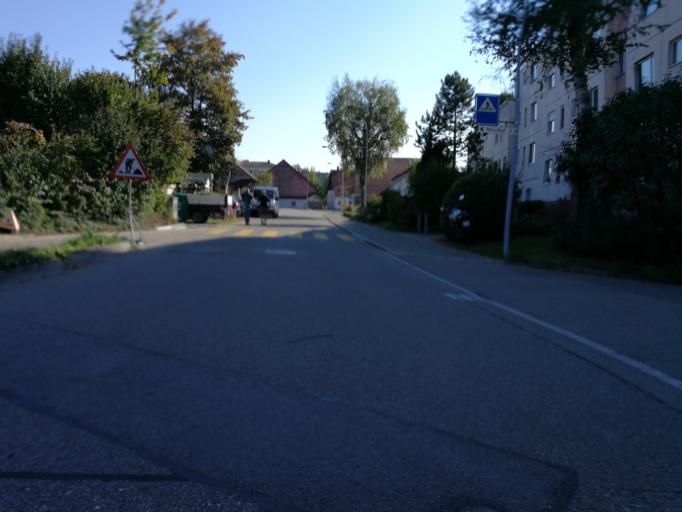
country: CH
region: Zurich
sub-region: Bezirk Uster
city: Monchaltorf
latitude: 47.3113
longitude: 8.7190
